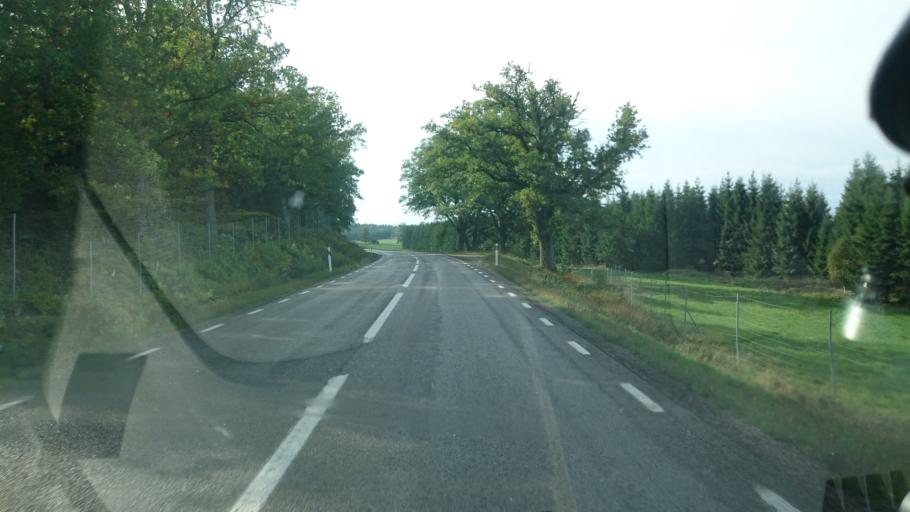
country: SE
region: Vaestra Goetaland
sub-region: Alingsas Kommun
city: Sollebrunn
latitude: 58.1563
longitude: 12.4220
